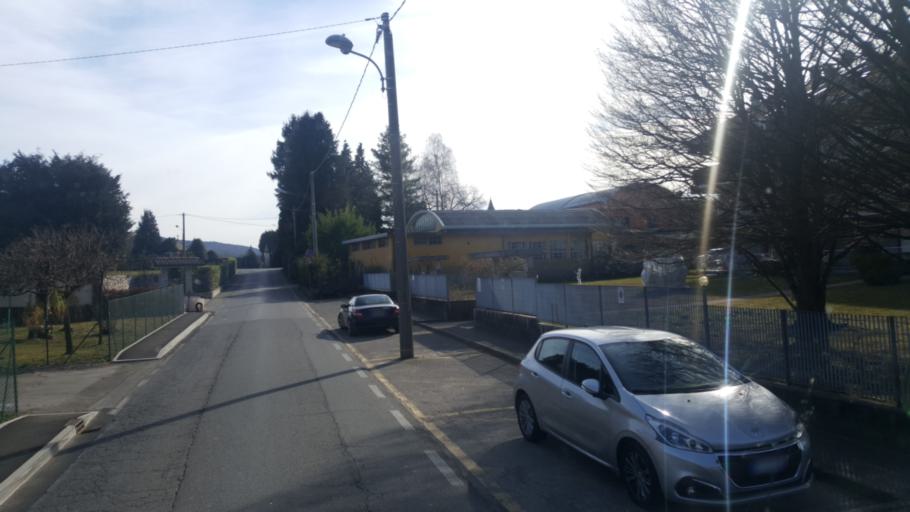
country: IT
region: Lombardy
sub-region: Provincia di Varese
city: Cadrezzate
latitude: 45.8008
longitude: 8.6457
